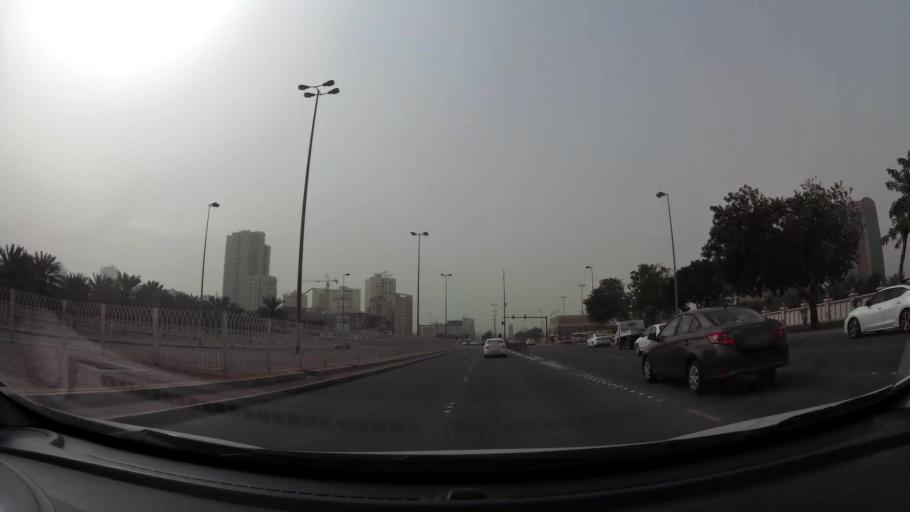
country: BH
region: Manama
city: Manama
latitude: 26.2181
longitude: 50.5970
